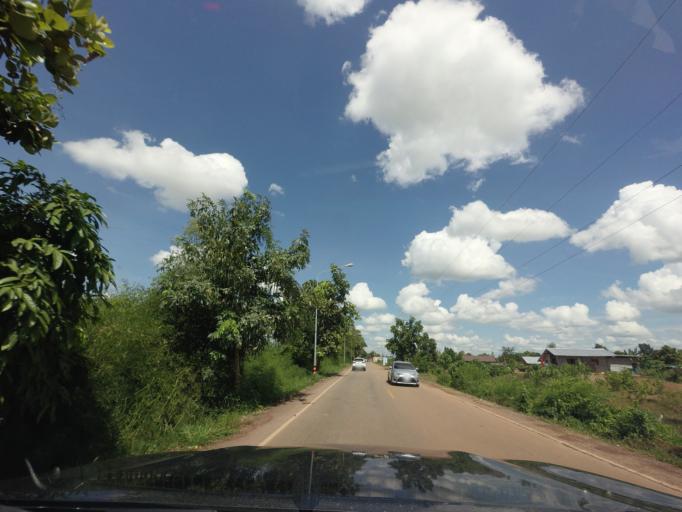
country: TH
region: Changwat Udon Thani
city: Ban Dung
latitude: 17.7398
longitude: 103.3503
